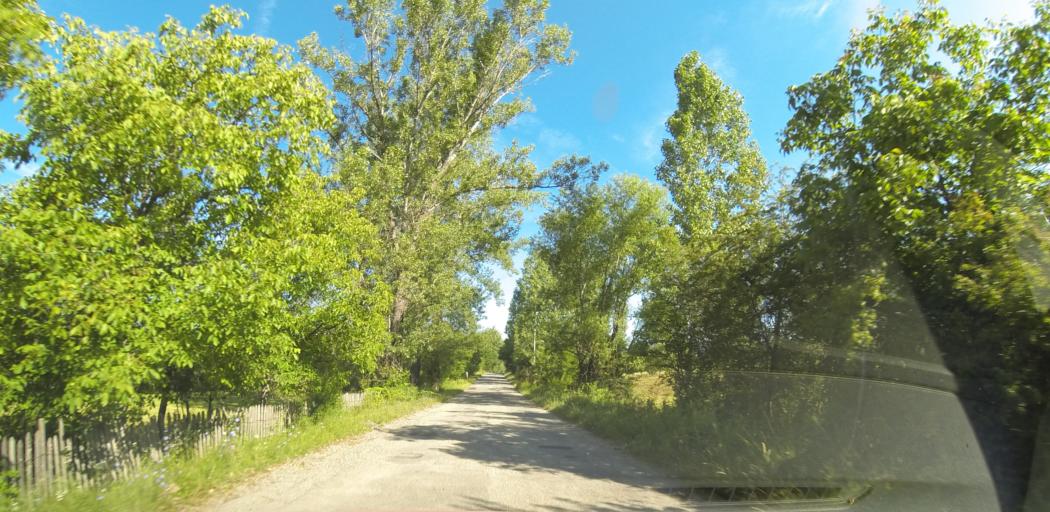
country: RO
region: Gorj
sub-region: Comuna Polovragi
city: Polovragi
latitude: 45.1696
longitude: 23.8572
